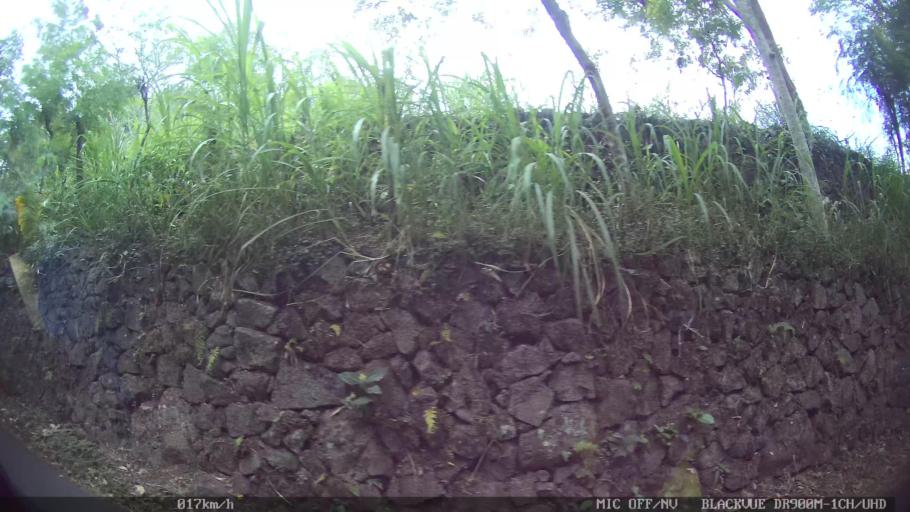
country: ID
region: Central Java
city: Candi Prambanan
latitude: -7.8022
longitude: 110.5210
